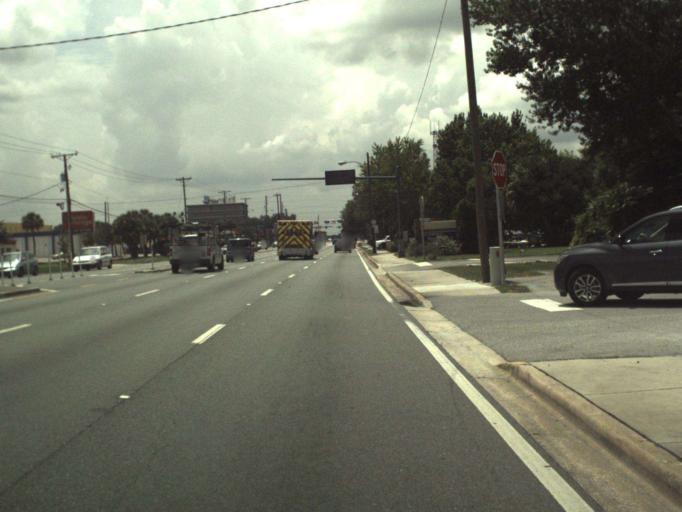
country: US
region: Florida
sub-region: Seminole County
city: Altamonte Springs
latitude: 28.6632
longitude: -81.3539
